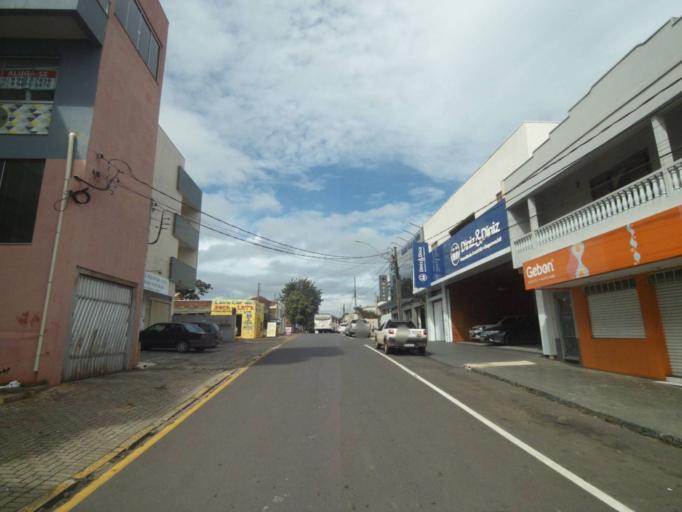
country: BR
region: Parana
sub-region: Telemaco Borba
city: Telemaco Borba
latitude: -24.3279
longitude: -50.6243
